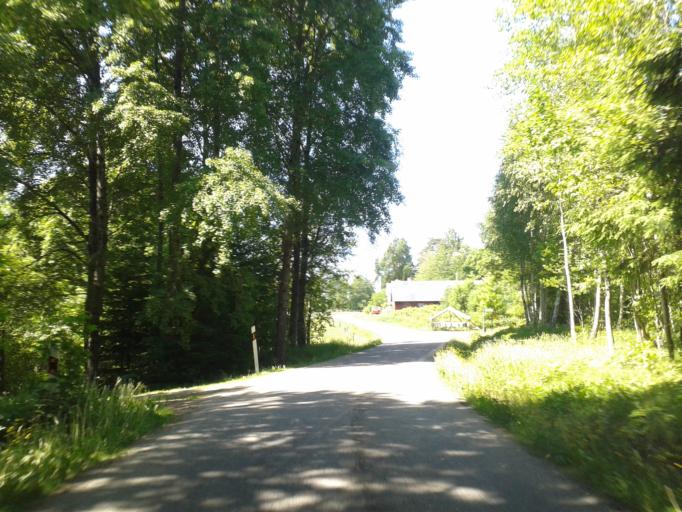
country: SE
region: Vaestra Goetaland
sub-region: Orust
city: Henan
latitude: 58.2785
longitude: 11.7552
